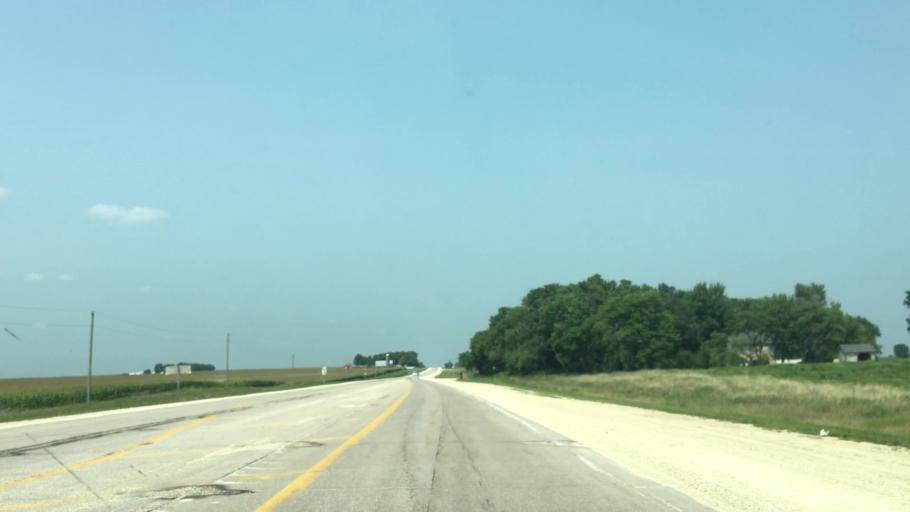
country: US
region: Iowa
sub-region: Fayette County
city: Fayette
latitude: 42.7604
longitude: -91.8044
